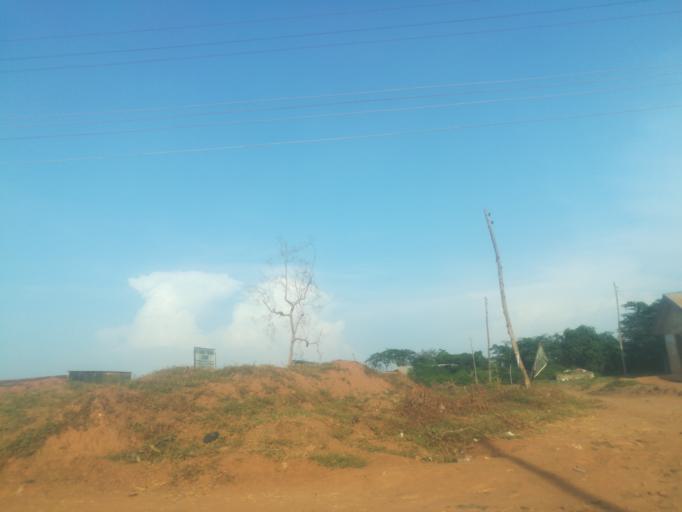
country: NG
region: Oyo
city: Moniya
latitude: 7.5605
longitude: 3.8870
